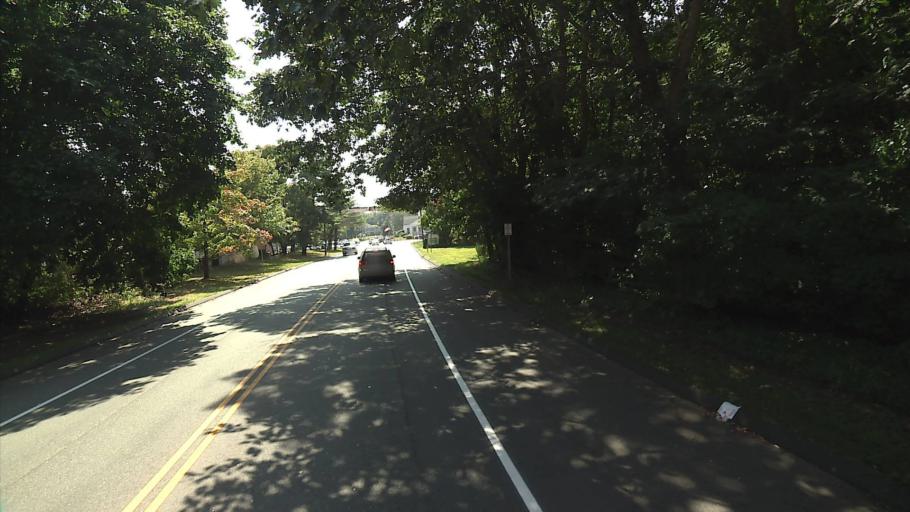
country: US
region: Connecticut
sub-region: New Haven County
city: Madison
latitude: 41.2806
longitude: -72.5990
